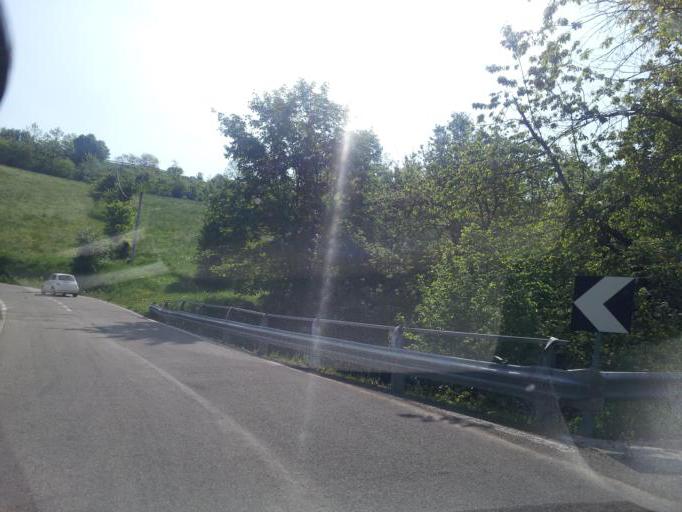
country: IT
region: Emilia-Romagna
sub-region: Provincia di Reggio Emilia
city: Villa Minozzo
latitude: 44.3684
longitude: 10.4627
